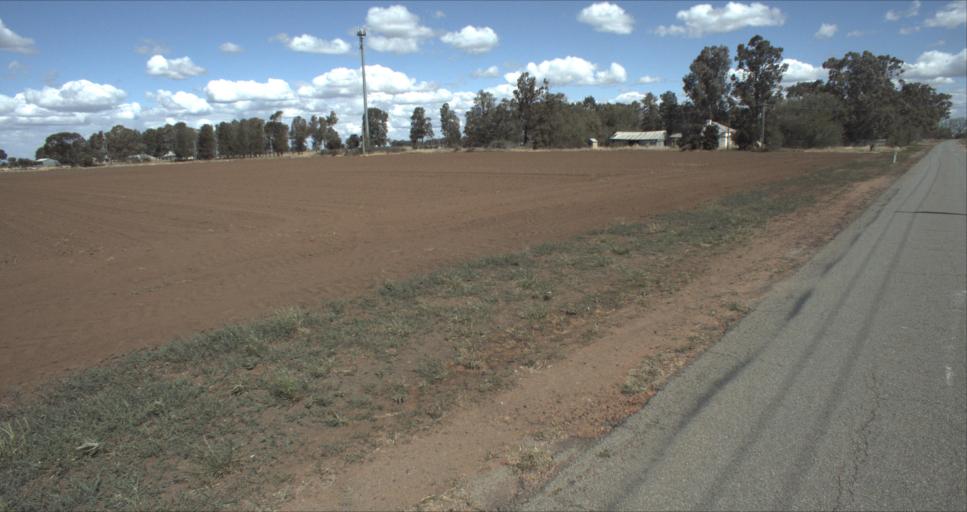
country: AU
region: New South Wales
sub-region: Leeton
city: Leeton
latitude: -34.5126
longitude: 146.2522
